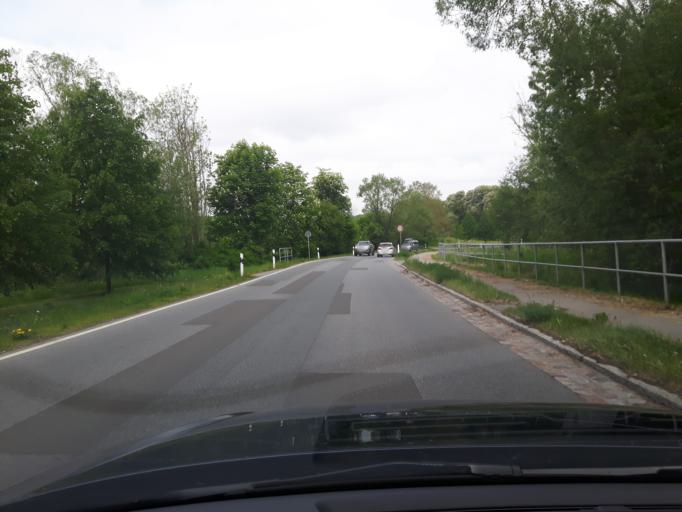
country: DE
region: Mecklenburg-Vorpommern
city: Gross Wokern
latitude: 53.6524
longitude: 12.4977
